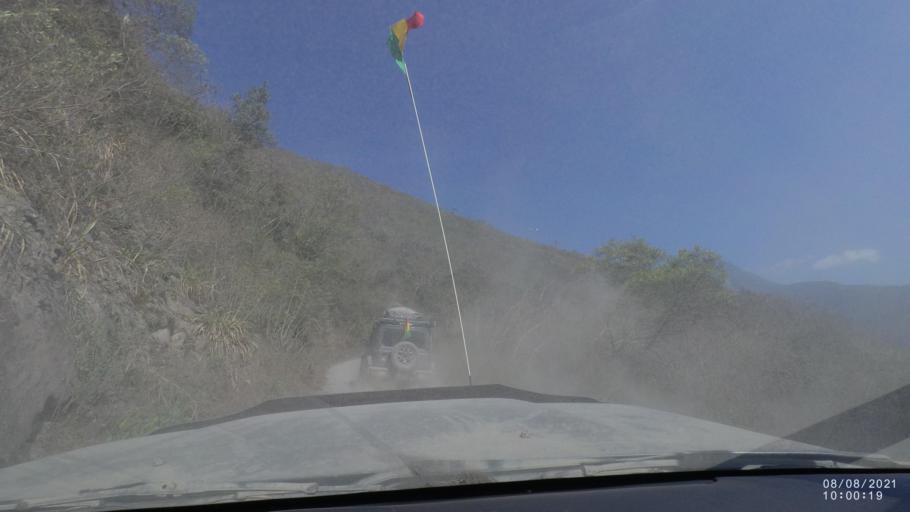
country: BO
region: La Paz
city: Quime
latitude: -16.6463
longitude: -66.7257
